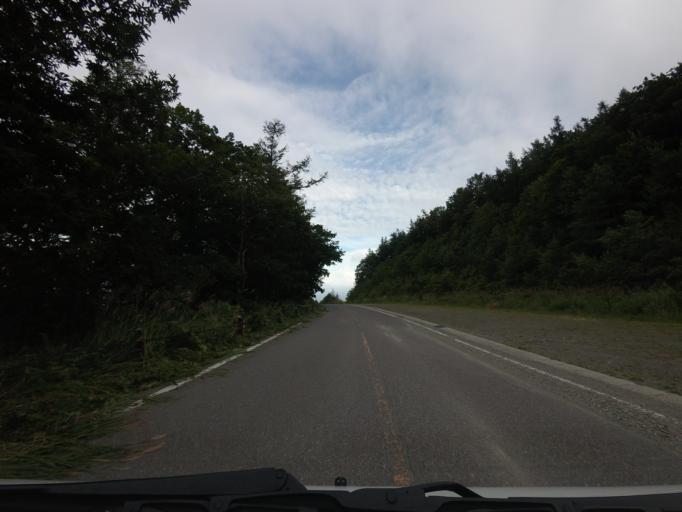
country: JP
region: Fukushima
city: Nihommatsu
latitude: 37.6225
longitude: 140.3274
